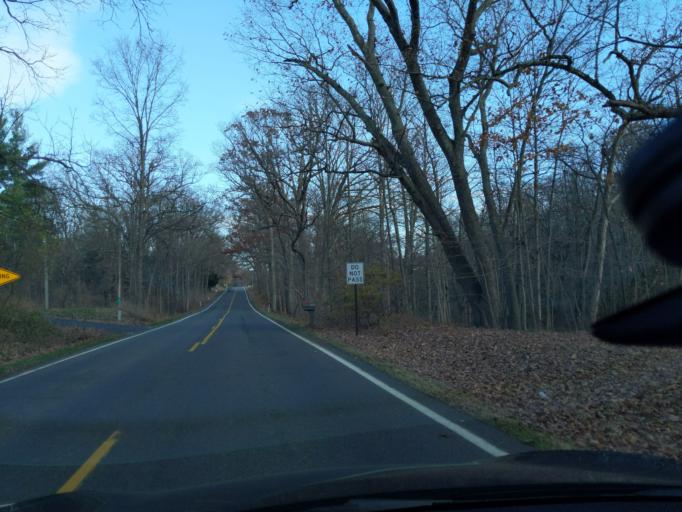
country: US
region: Michigan
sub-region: Ingham County
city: Haslett
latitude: 42.7154
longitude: -84.3452
